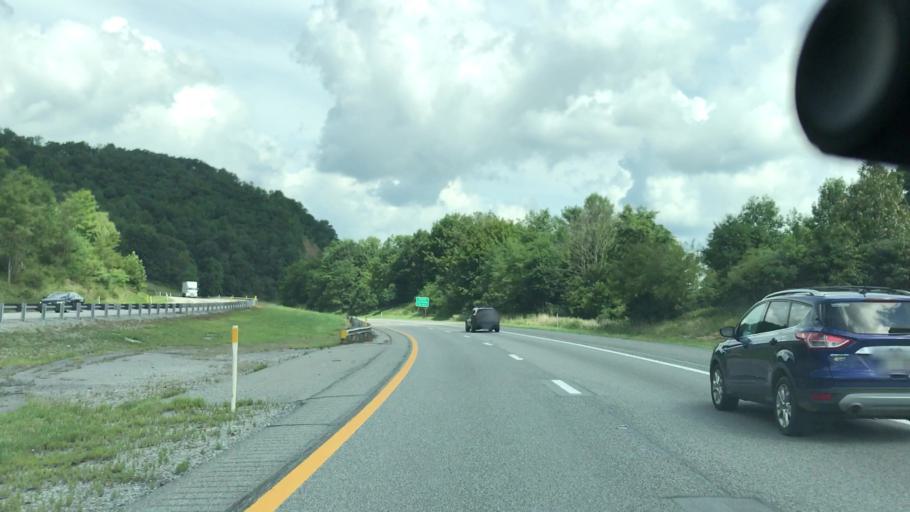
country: US
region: West Virginia
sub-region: Mercer County
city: Athens
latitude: 37.4598
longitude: -81.0643
